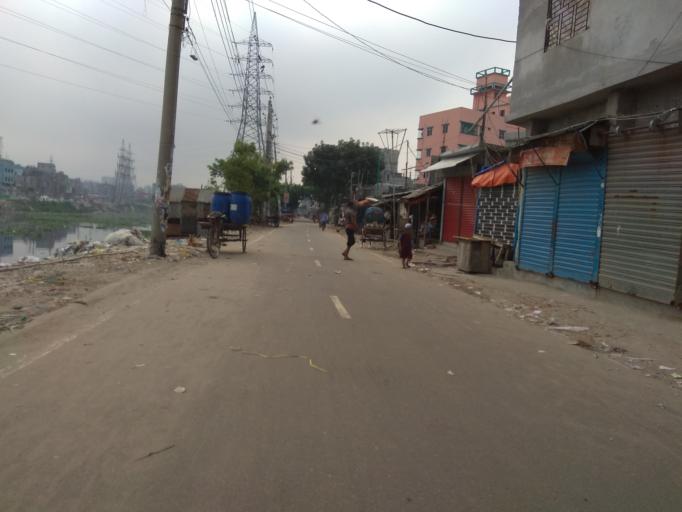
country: BD
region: Dhaka
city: Azimpur
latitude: 23.7110
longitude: 90.3857
